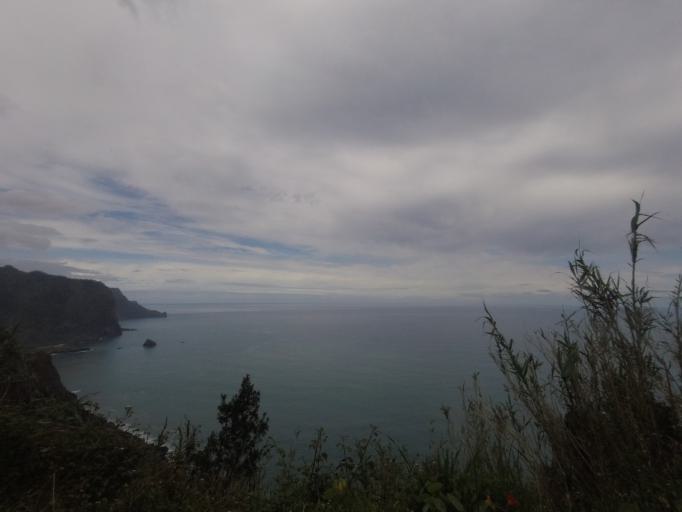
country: PT
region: Madeira
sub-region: Machico
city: Canical
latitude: 32.7617
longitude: -16.8036
